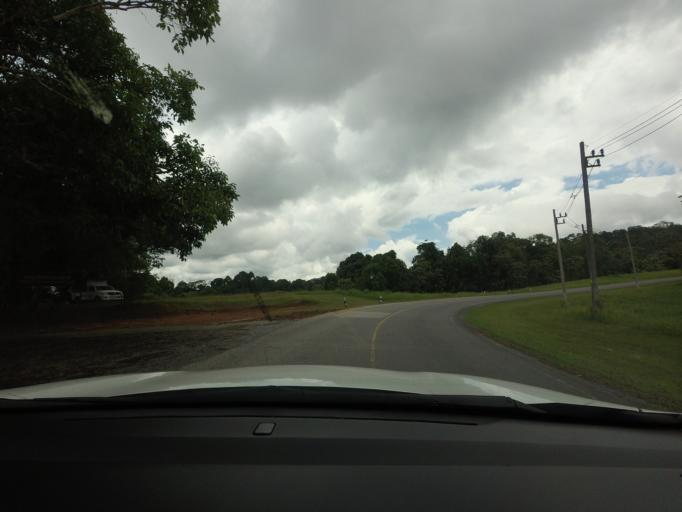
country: TH
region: Nakhon Ratchasima
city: Pak Chong
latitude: 14.4510
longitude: 101.3678
